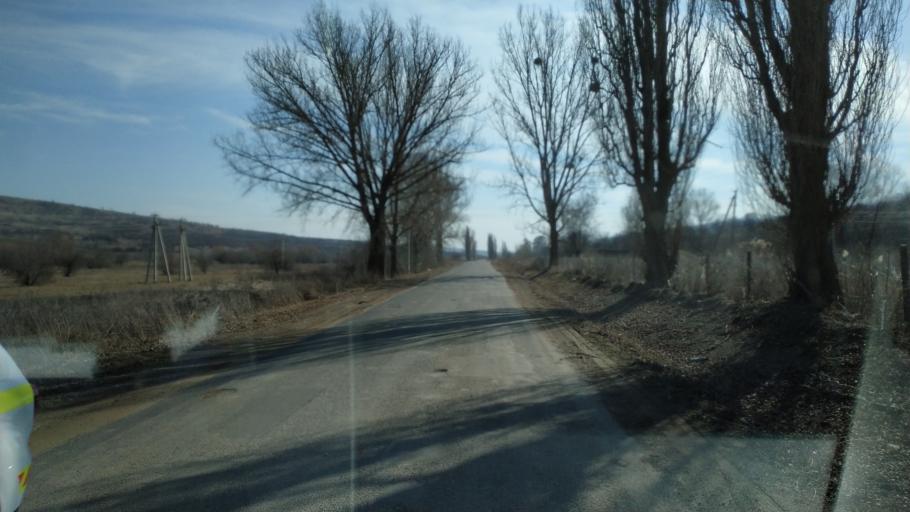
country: MD
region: Nisporeni
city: Nisporeni
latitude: 47.1598
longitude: 28.1046
